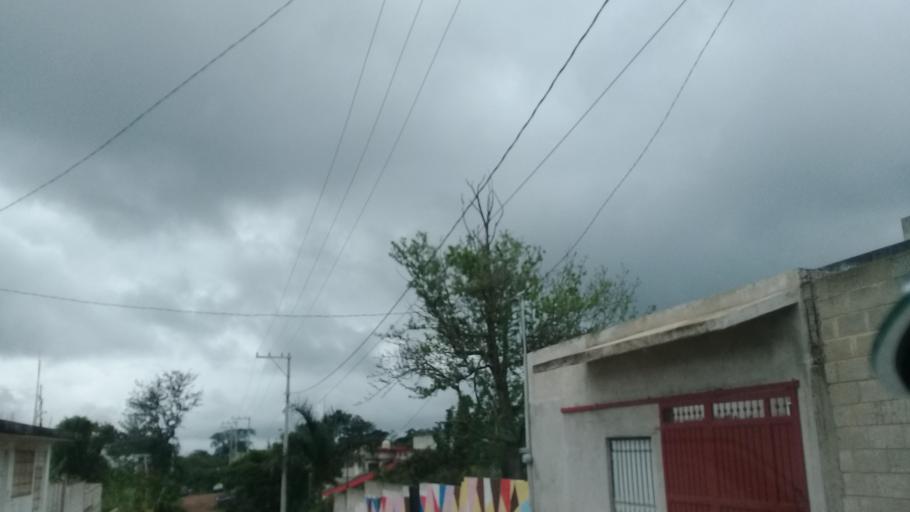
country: MX
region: Veracruz
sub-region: Emiliano Zapata
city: Las Trancas
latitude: 19.4965
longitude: -96.8652
